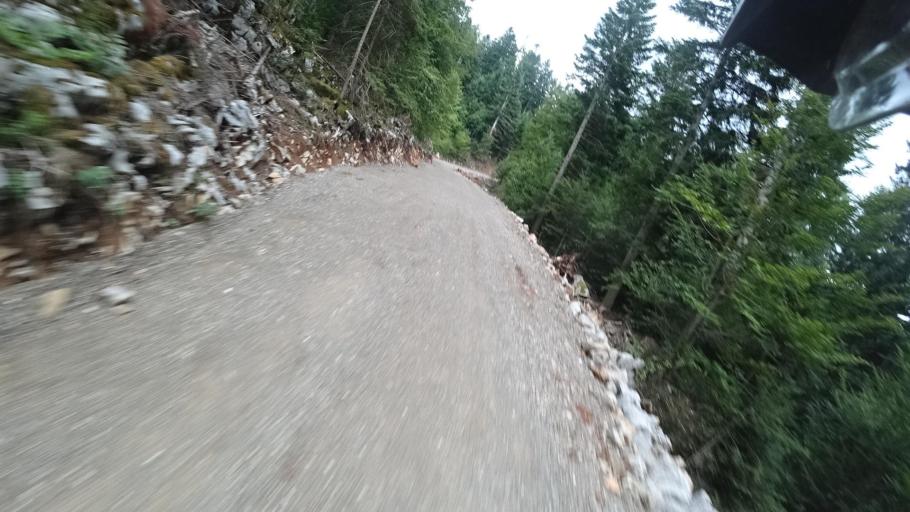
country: HR
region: Licko-Senjska
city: Senj
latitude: 45.1210
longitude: 14.9729
